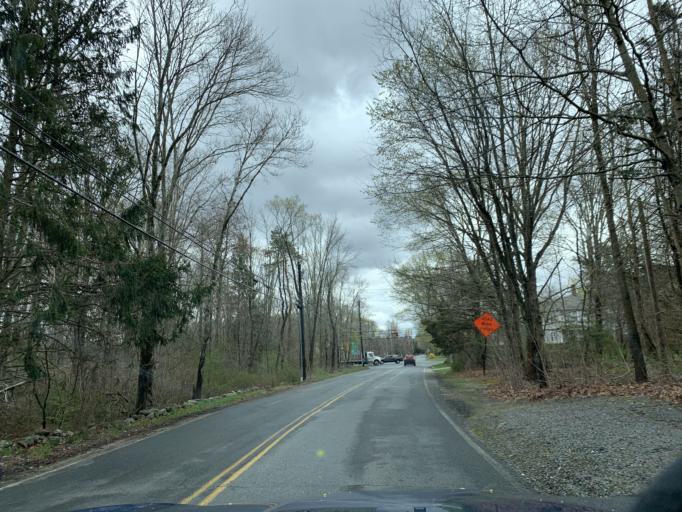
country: US
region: Massachusetts
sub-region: Bristol County
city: Rehoboth
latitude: 41.8701
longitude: -71.2031
